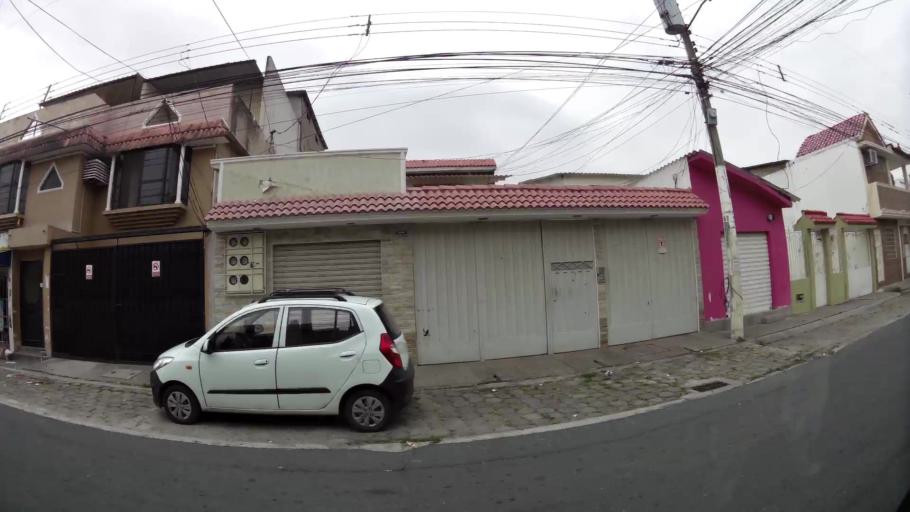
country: EC
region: Guayas
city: Eloy Alfaro
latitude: -2.1407
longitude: -79.9054
